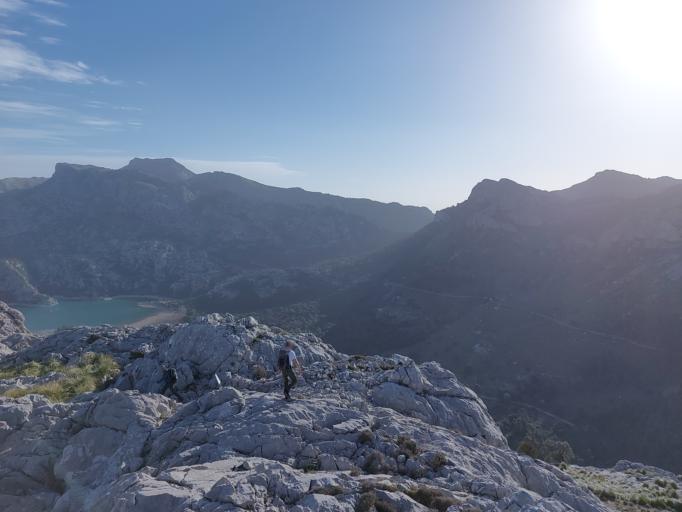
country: ES
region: Balearic Islands
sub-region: Illes Balears
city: Fornalutx
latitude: 39.7963
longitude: 2.7995
